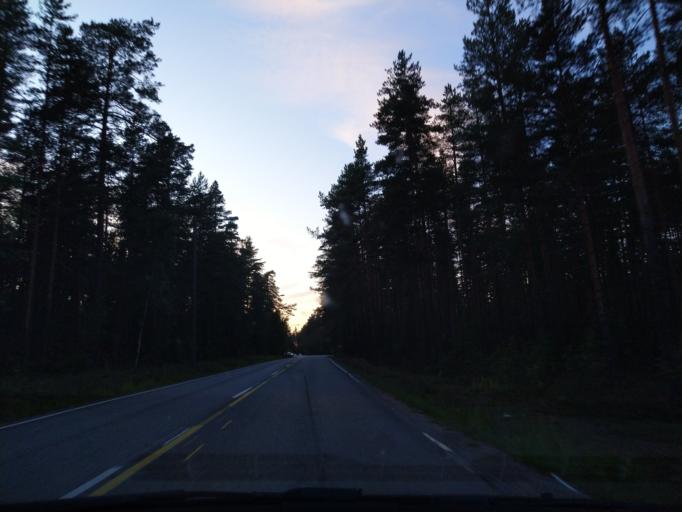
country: FI
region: Uusimaa
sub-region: Helsinki
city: Tuusula
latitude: 60.3549
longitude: 25.0132
